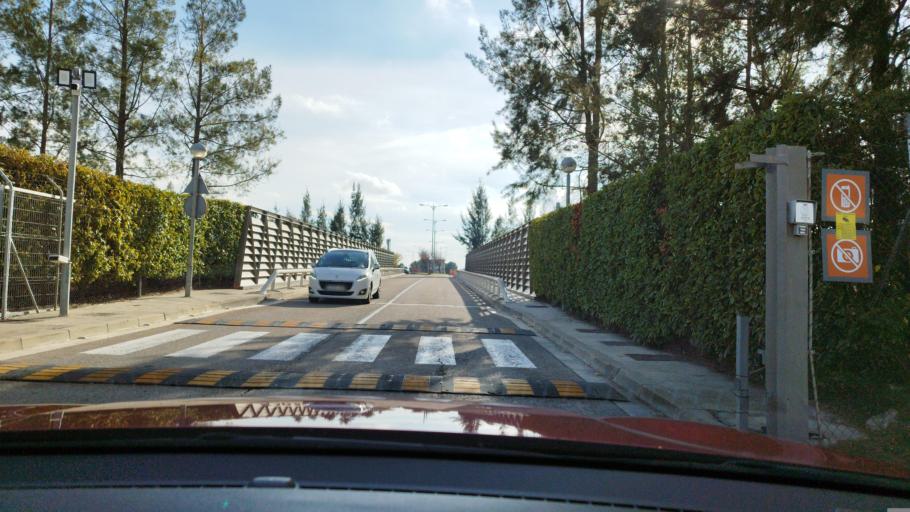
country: ES
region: Catalonia
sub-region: Provincia de Tarragona
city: Santa Oliva
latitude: 41.2686
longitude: 1.5235
